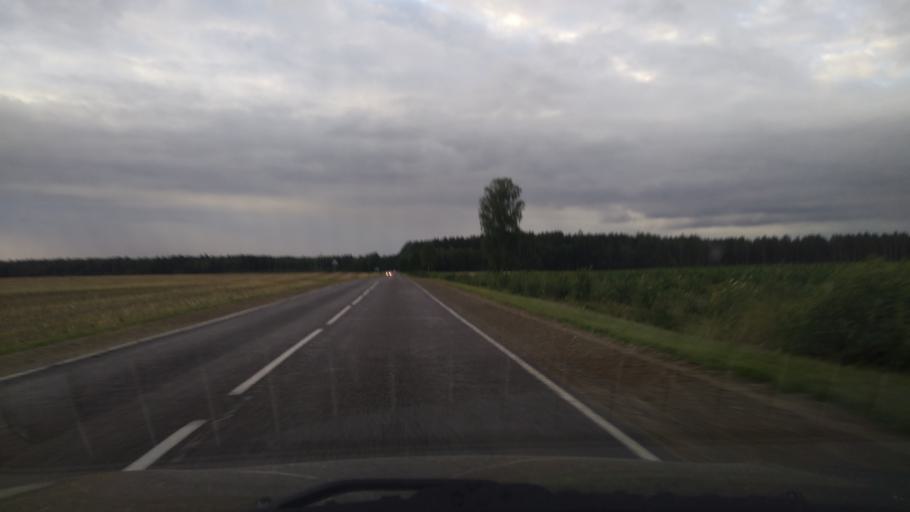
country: BY
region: Brest
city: Byaroza
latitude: 52.3992
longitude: 25.0047
